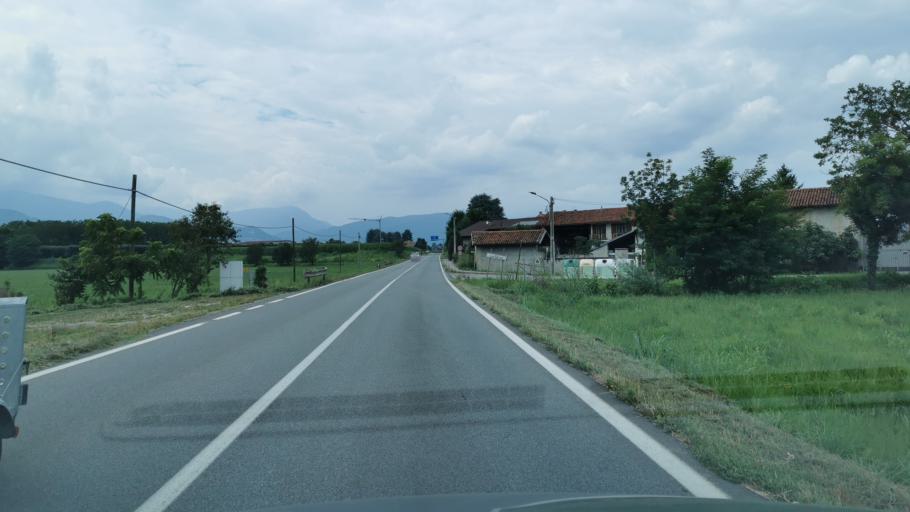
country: IT
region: Piedmont
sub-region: Provincia di Torino
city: Garzigliana
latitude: 44.8371
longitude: 7.3586
